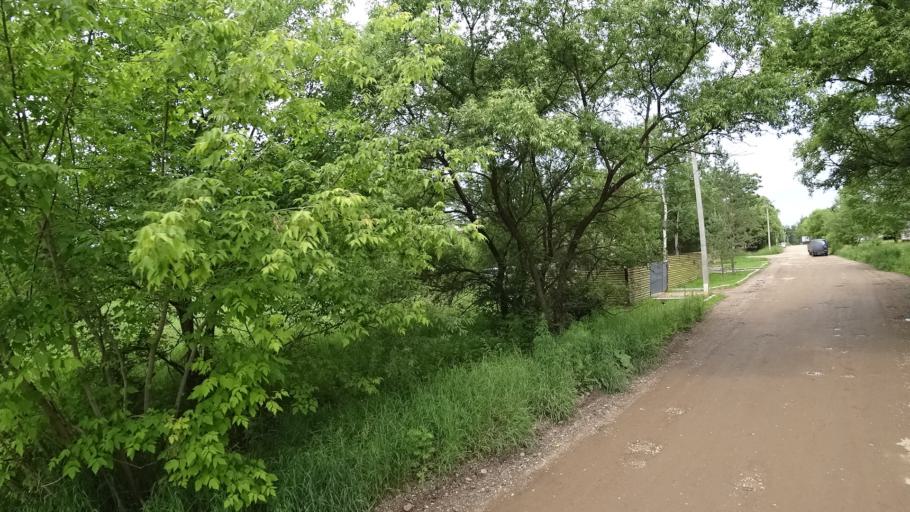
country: RU
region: Primorskiy
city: Novosysoyevka
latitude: 44.2263
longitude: 133.3618
